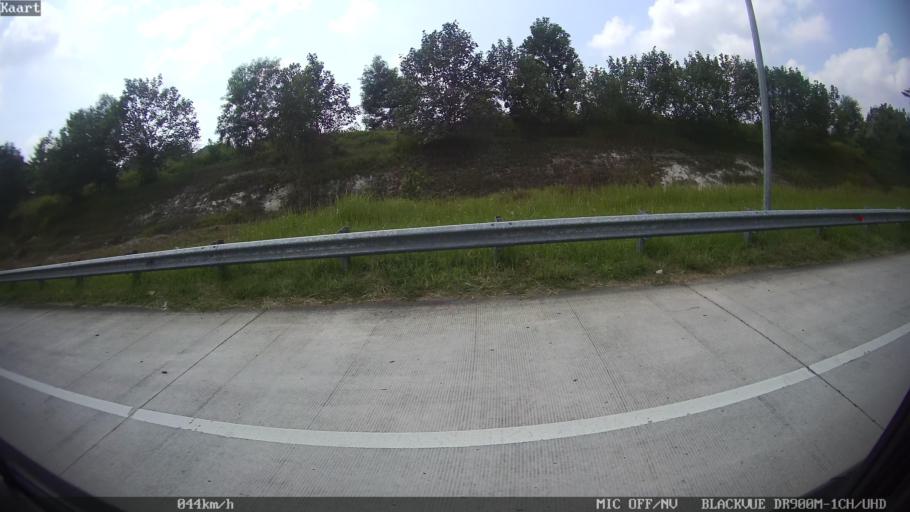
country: ID
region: Lampung
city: Natar
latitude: -5.2751
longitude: 105.2173
